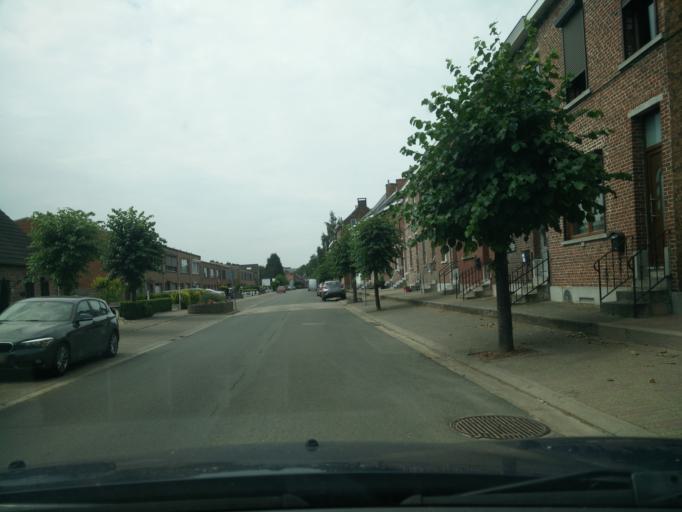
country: BE
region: Wallonia
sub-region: Province du Hainaut
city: Braine-le-Comte
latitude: 50.6147
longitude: 4.1434
